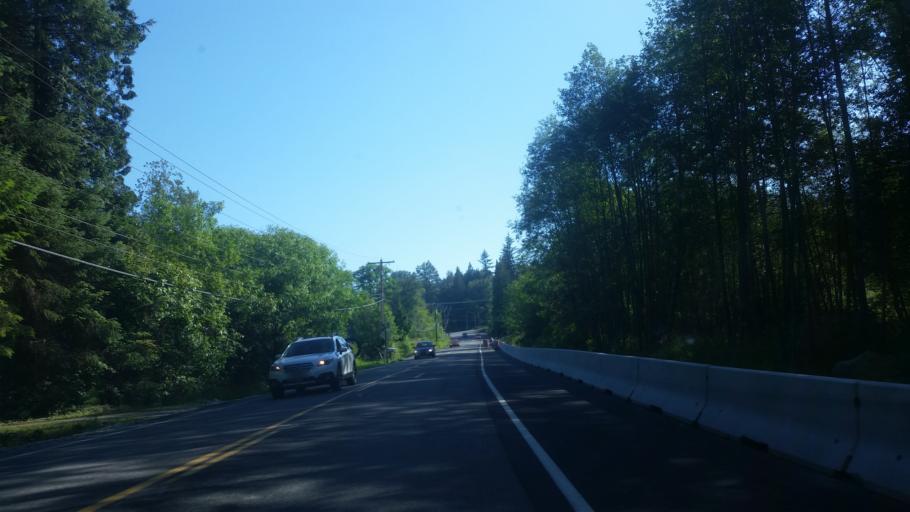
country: US
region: Washington
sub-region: Snohomish County
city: Cathcart
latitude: 47.8367
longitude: -122.1053
